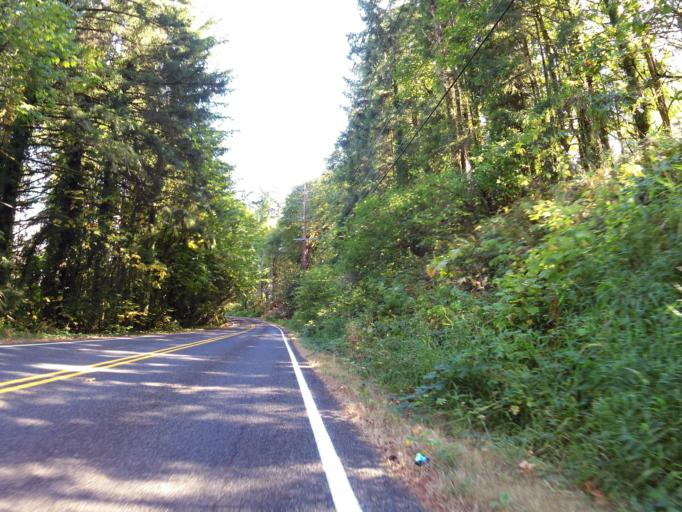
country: US
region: Washington
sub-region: Thurston County
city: Olympia
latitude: 47.0639
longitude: -123.0161
